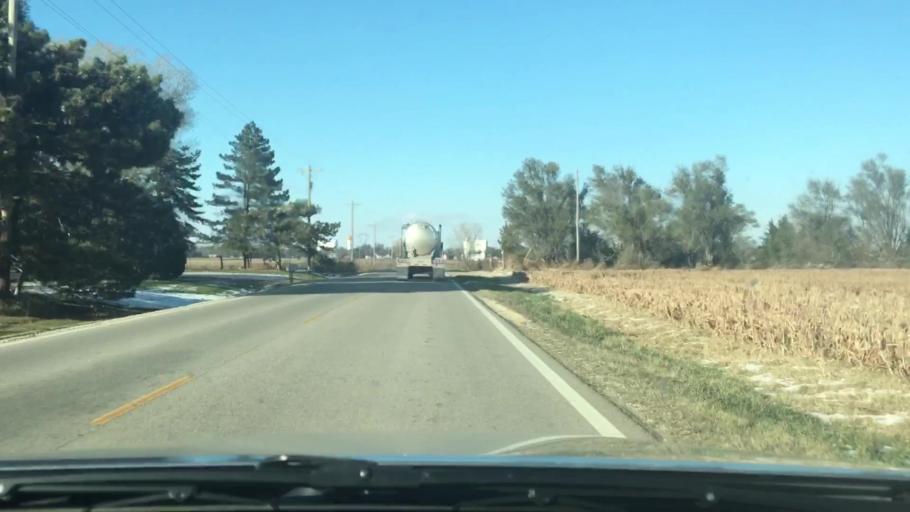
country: US
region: Kansas
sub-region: Rice County
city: Sterling
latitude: 38.1911
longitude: -98.2068
